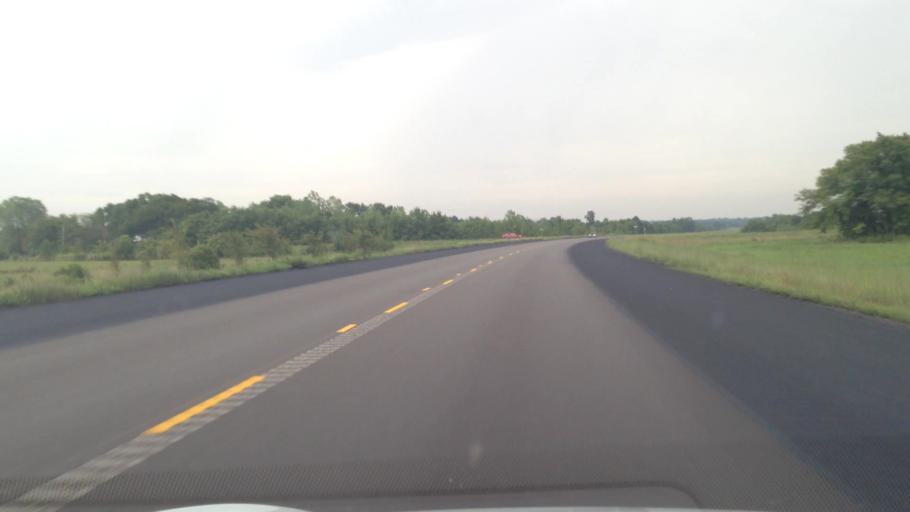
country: US
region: Kansas
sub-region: Cherokee County
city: Baxter Springs
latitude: 37.0468
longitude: -94.7138
